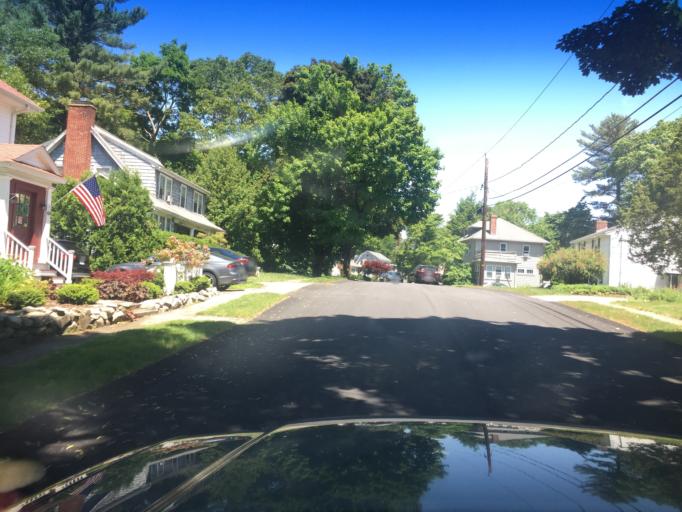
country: US
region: Massachusetts
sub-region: Norfolk County
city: Norwood
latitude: 42.2223
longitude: -71.1888
